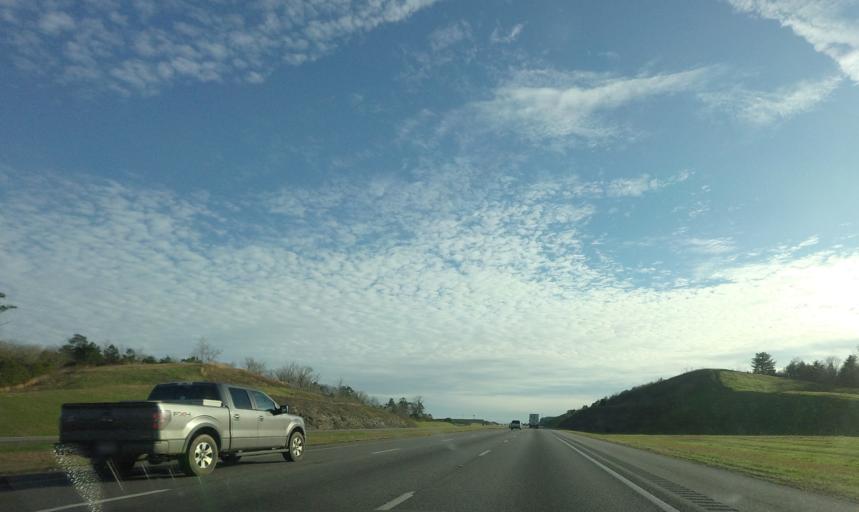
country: US
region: Alabama
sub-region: Walker County
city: Cordova
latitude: 33.7669
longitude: -87.2076
